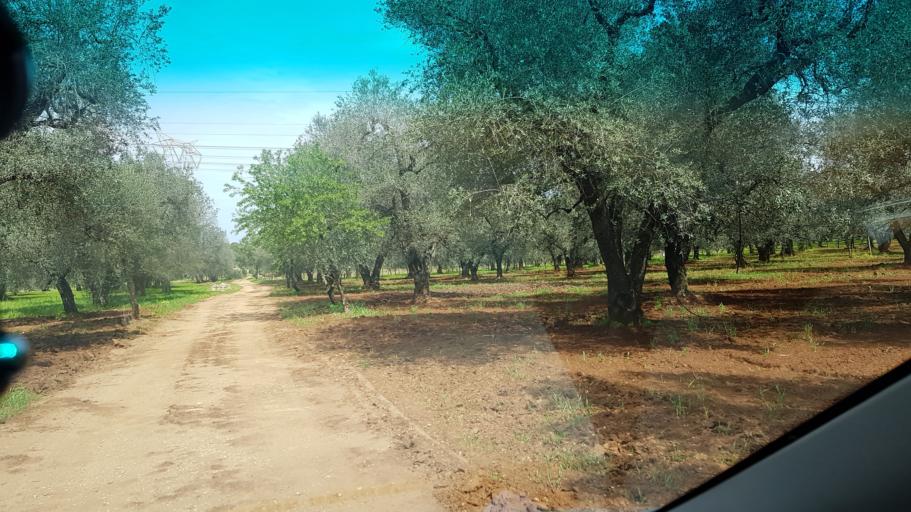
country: IT
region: Apulia
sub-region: Provincia di Brindisi
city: Mesagne
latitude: 40.6044
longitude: 17.8537
